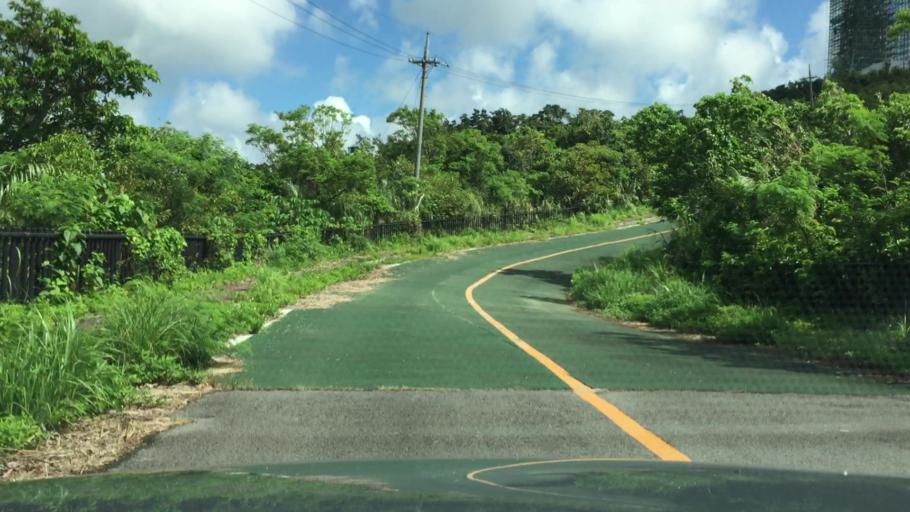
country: JP
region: Okinawa
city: Ishigaki
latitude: 24.3769
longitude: 124.1642
